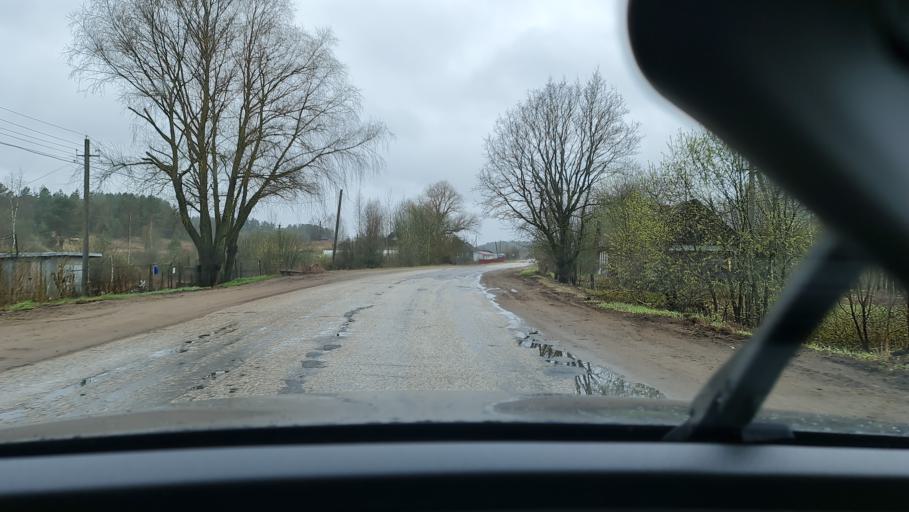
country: RU
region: Novgorod
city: Valday
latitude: 58.0360
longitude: 32.9442
